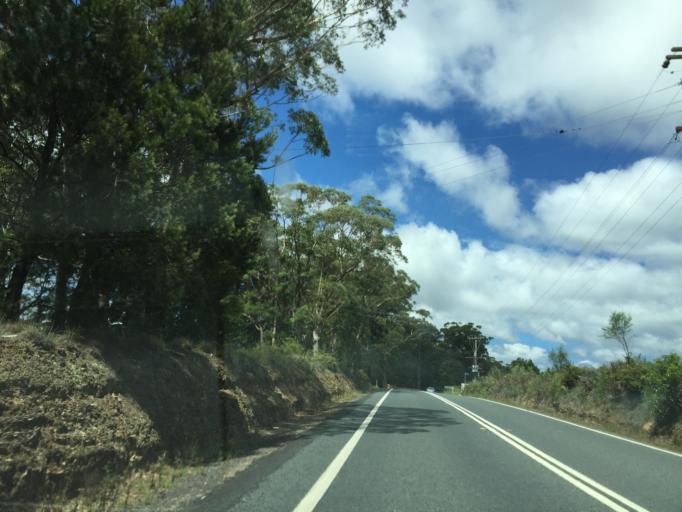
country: AU
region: New South Wales
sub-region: Blue Mountains Municipality
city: Hazelbrook
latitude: -33.5103
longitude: 150.4937
